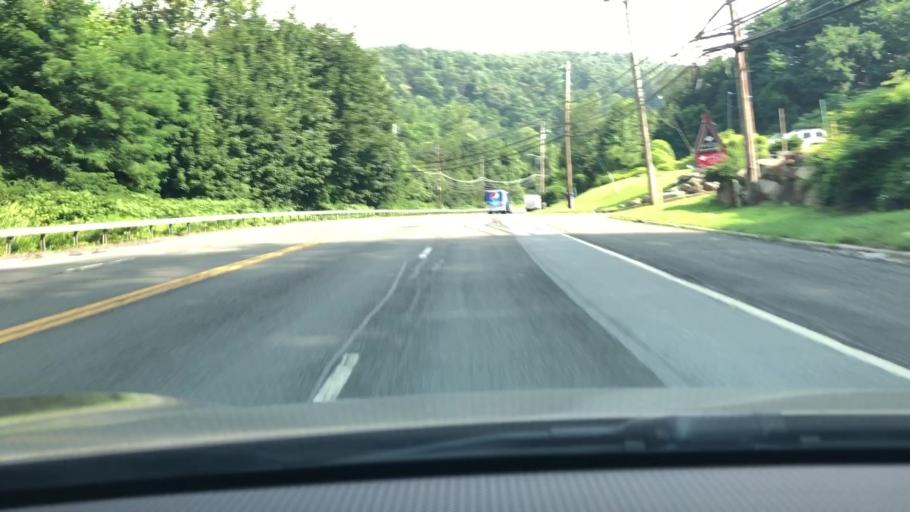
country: US
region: New York
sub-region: Westchester County
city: Hawthorne
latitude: 41.0888
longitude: -73.8197
